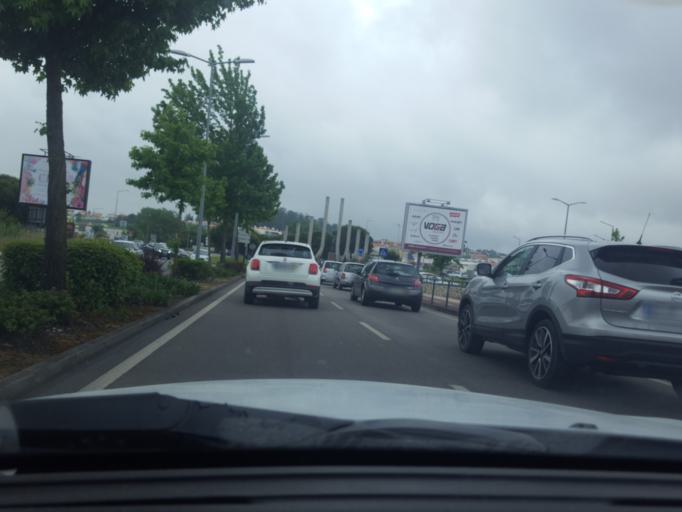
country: PT
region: Leiria
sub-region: Leiria
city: Leiria
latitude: 39.7391
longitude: -8.8166
